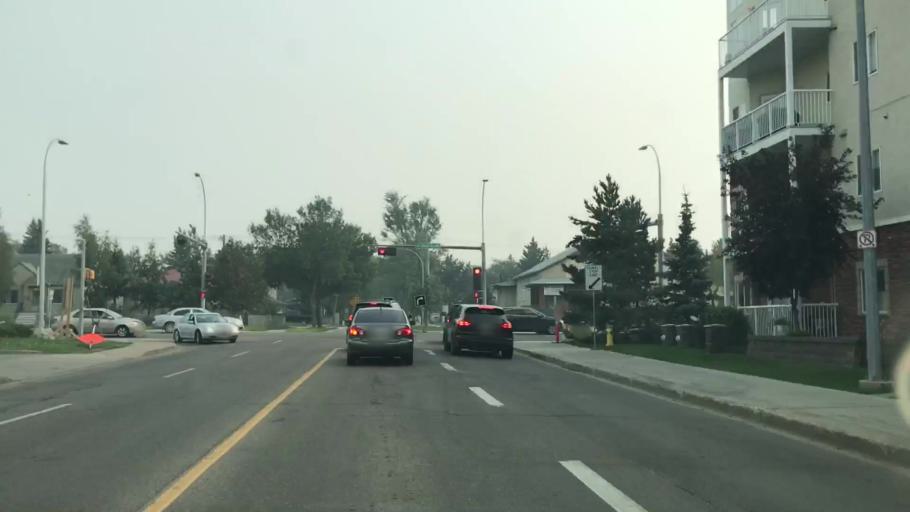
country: CA
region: Alberta
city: Edmonton
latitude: 53.5186
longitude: -113.4583
